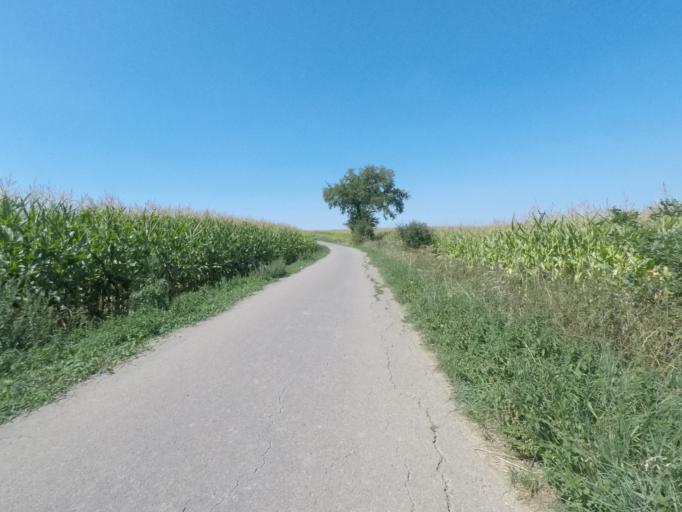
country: LU
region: Luxembourg
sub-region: Canton de Capellen
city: Garnich
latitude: 49.6334
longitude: 5.9299
